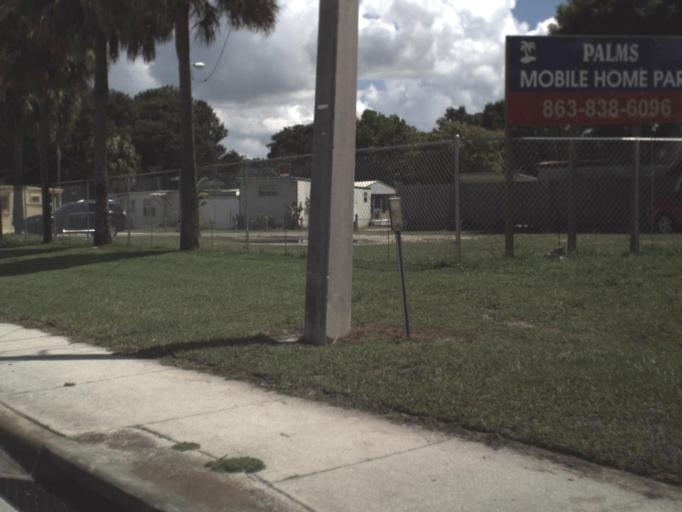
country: US
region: Florida
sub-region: Polk County
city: Auburndale
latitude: 28.0584
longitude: -81.8110
